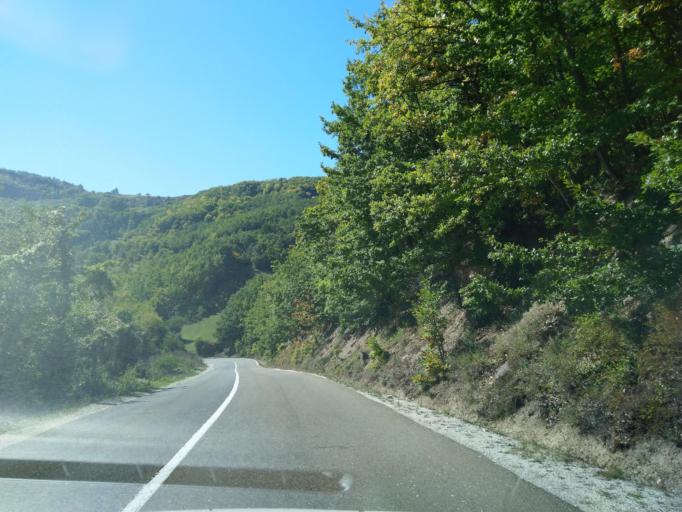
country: RS
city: Sokolovica
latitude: 43.2525
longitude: 20.2548
